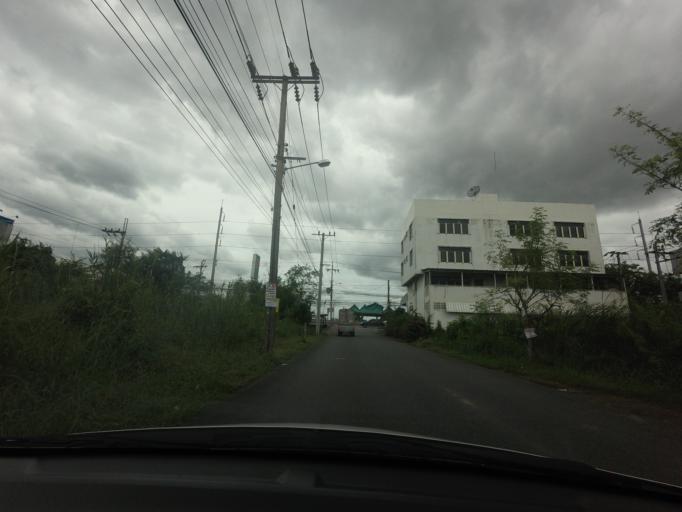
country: TH
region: Bangkok
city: Min Buri
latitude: 13.7753
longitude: 100.7469
